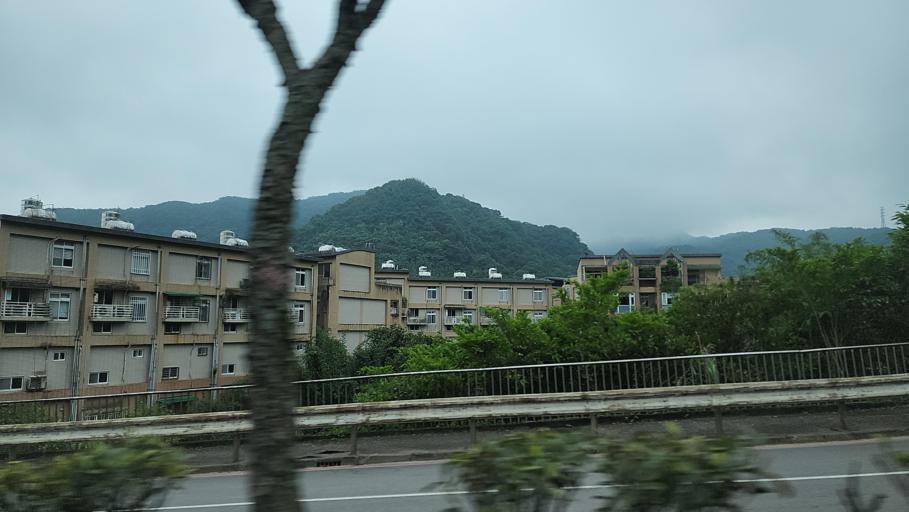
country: TW
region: Taiwan
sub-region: Keelung
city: Keelung
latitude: 25.1604
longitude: 121.6945
